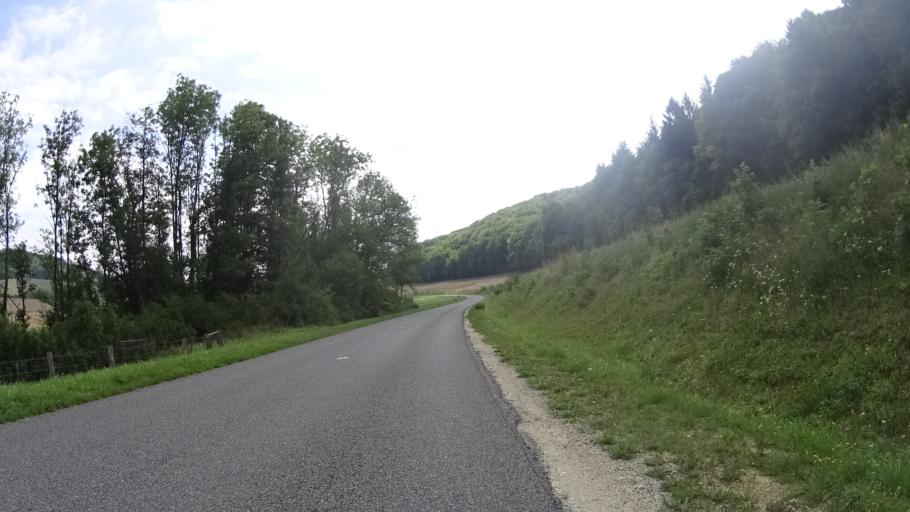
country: FR
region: Lorraine
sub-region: Departement de la Meuse
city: Ligny-en-Barrois
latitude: 48.7180
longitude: 5.3448
